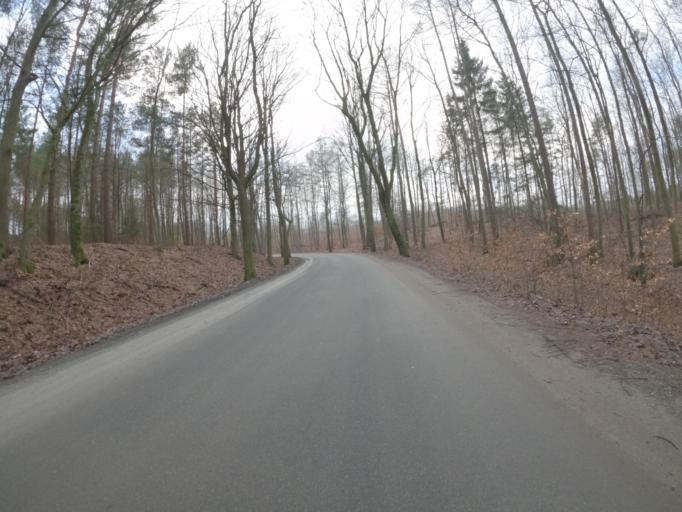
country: PL
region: West Pomeranian Voivodeship
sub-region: Koszalin
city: Koszalin
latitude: 54.2213
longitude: 16.2216
